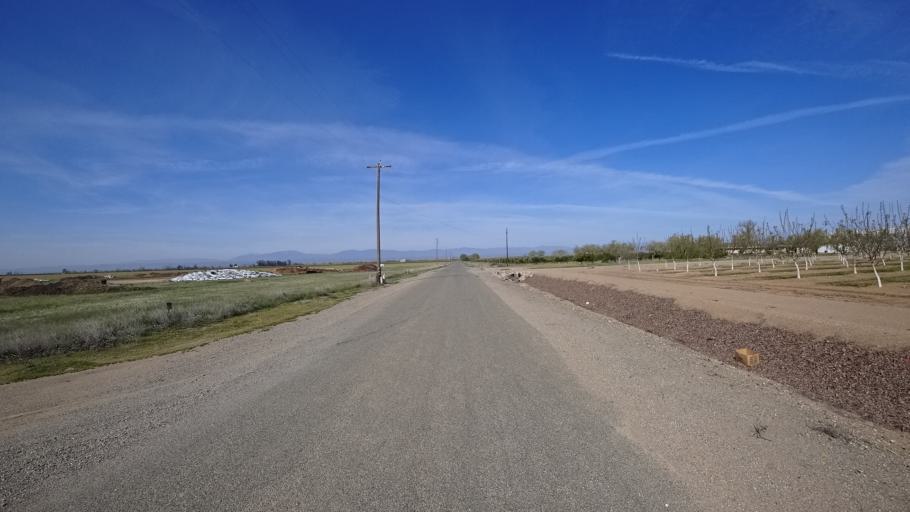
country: US
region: California
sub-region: Glenn County
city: Willows
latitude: 39.6114
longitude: -122.2223
